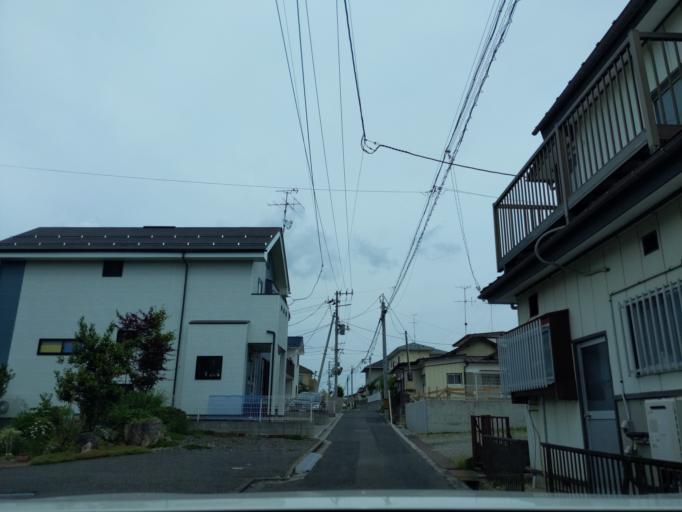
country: JP
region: Fukushima
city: Koriyama
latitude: 37.3923
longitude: 140.3447
